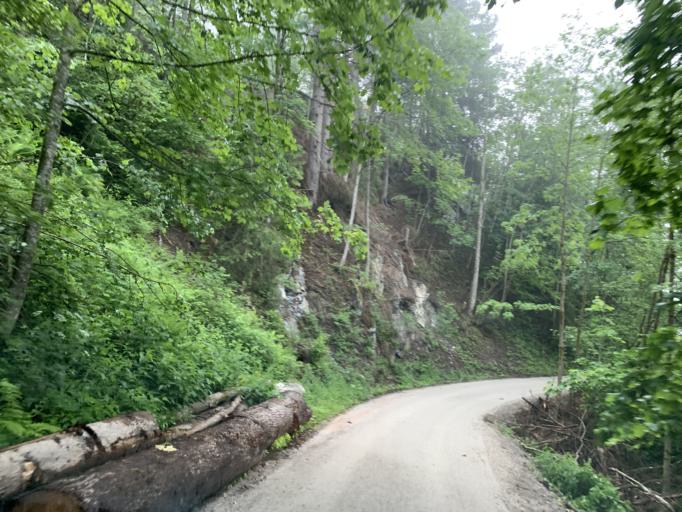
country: AT
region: Salzburg
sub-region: Politischer Bezirk Sankt Johann im Pongau
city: Forstau
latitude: 47.4062
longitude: 13.5738
